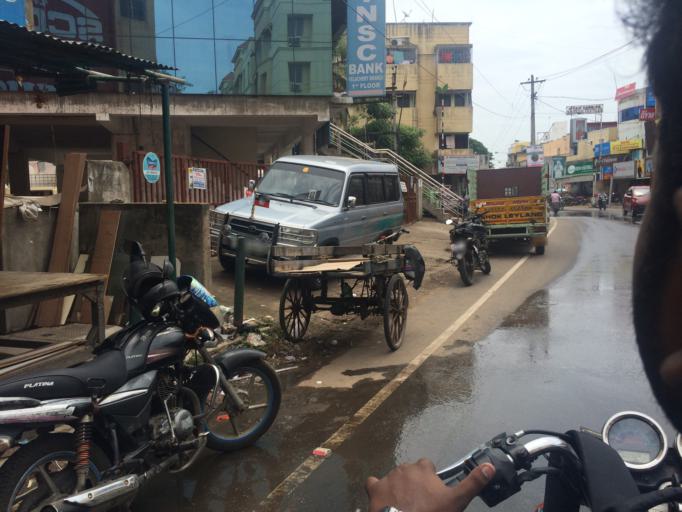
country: IN
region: Tamil Nadu
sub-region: Kancheepuram
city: Alandur
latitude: 12.9819
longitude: 80.2215
